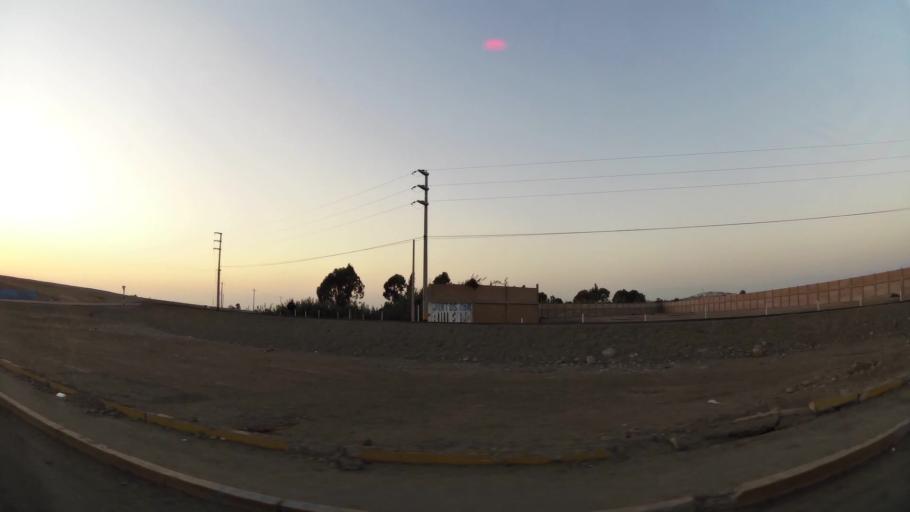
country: PE
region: Ica
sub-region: Provincia de Pisco
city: Villa Tupac Amaru
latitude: -13.7124
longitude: -76.1638
